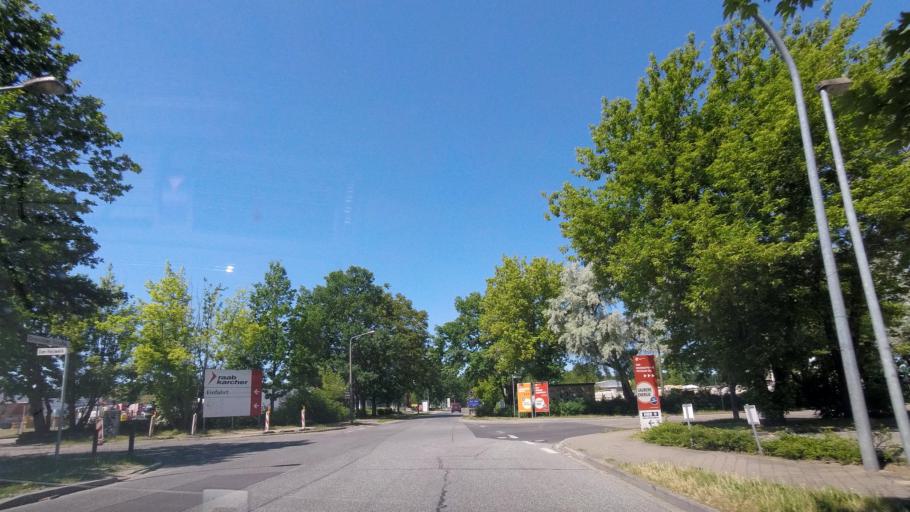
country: DE
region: Brandenburg
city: Potsdam
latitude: 52.3629
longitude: 13.1075
